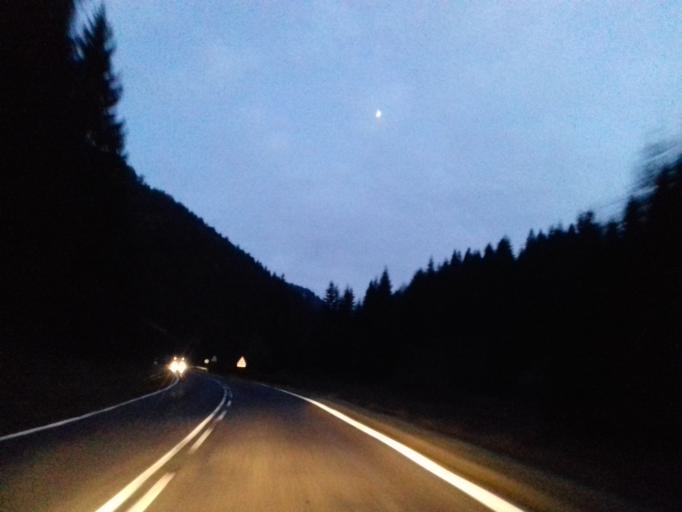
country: SK
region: Zilinsky
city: Ruzomberok
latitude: 48.9151
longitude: 19.2624
